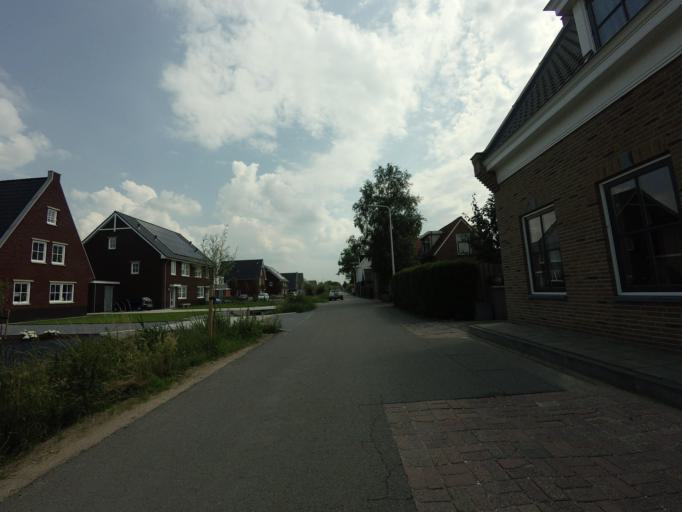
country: NL
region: South Holland
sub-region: Gemeente Vlist
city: Haastrecht
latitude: 51.9657
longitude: 4.7760
